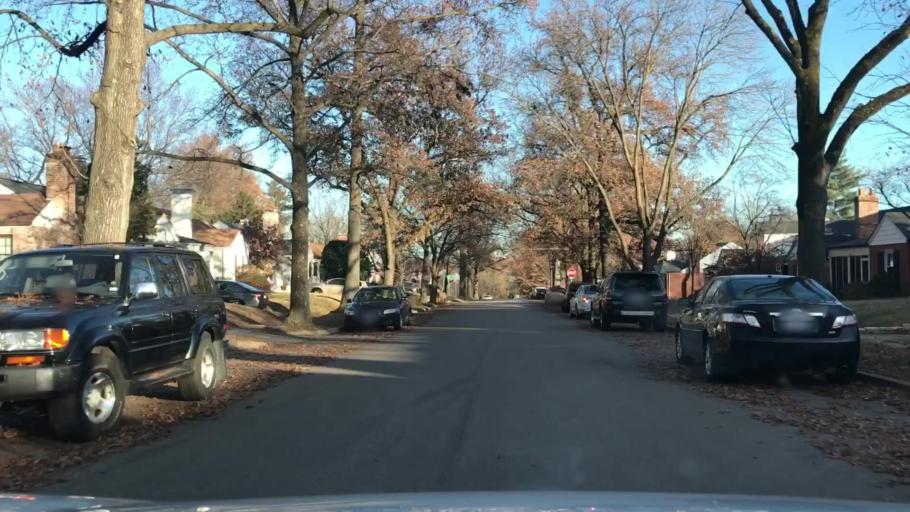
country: US
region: Missouri
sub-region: Saint Louis County
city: Brentwood
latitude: 38.6188
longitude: -90.3423
